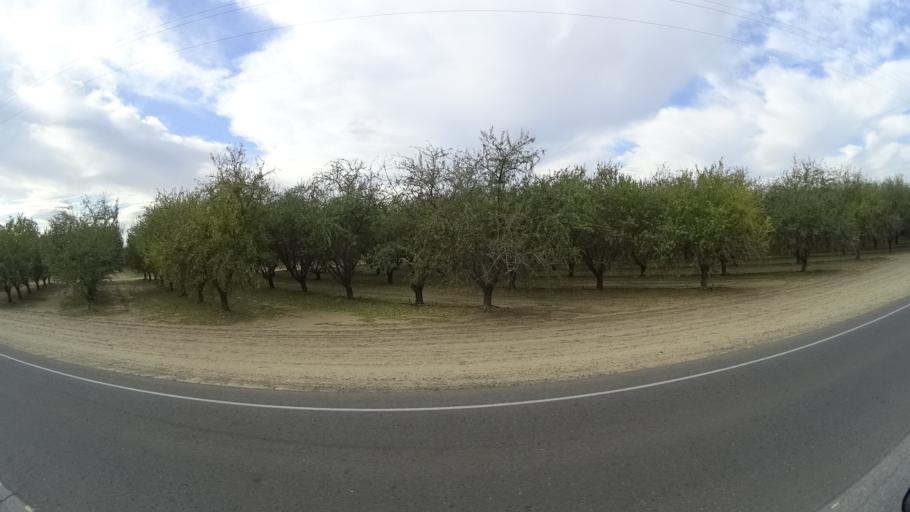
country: US
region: California
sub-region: Kern County
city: Rosedale
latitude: 35.4276
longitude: -119.1820
